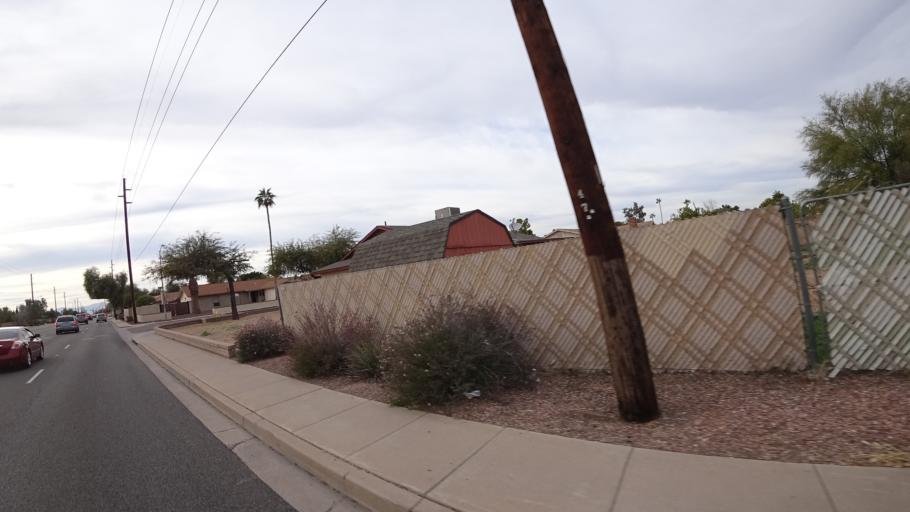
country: US
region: Arizona
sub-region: Maricopa County
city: Glendale
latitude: 33.5676
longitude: -112.1806
